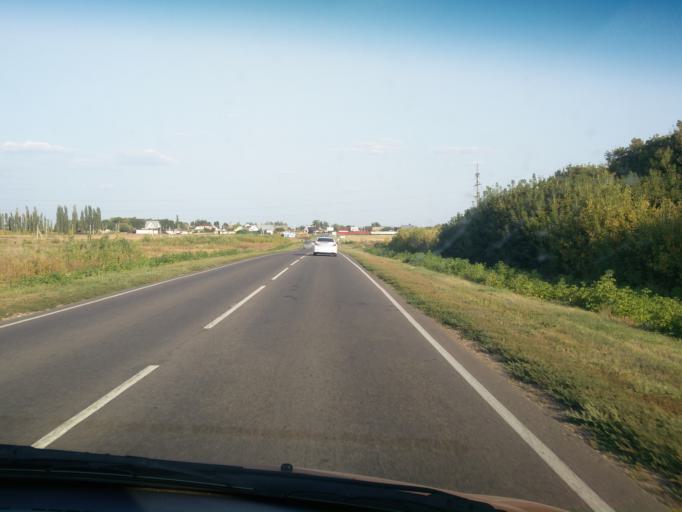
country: RU
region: Voronezj
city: Ramon'
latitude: 51.9355
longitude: 39.3389
